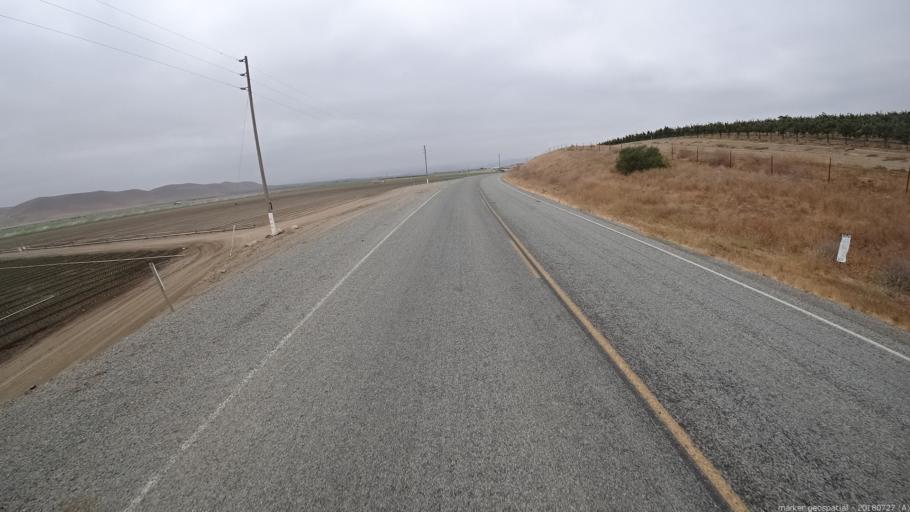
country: US
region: California
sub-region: Monterey County
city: King City
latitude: 36.2560
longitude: -121.0873
